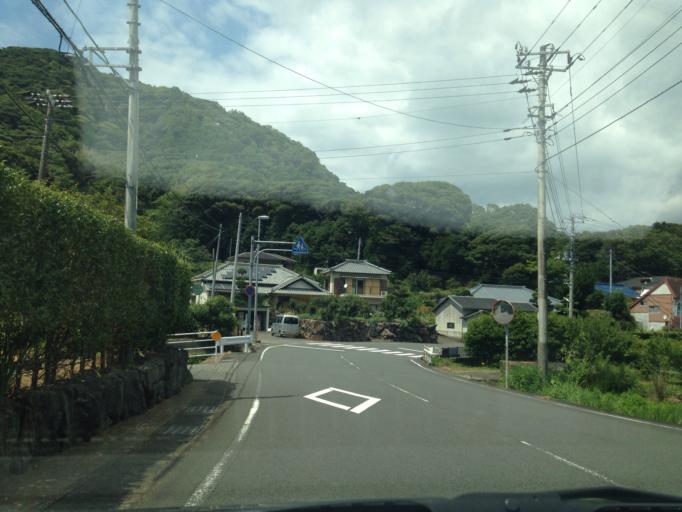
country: JP
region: Shizuoka
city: Shimoda
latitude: 34.6416
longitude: 138.8175
